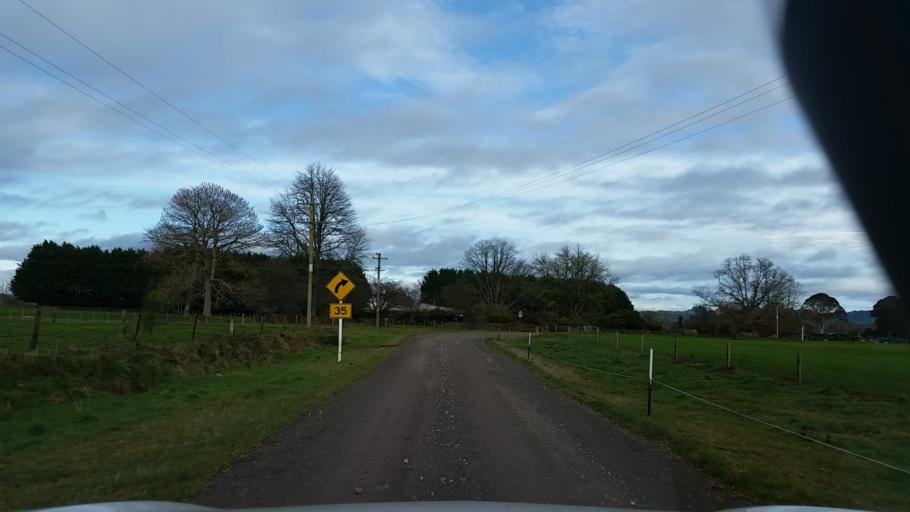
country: NZ
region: Bay of Plenty
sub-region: Rotorua District
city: Rotorua
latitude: -38.3964
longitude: 176.3882
